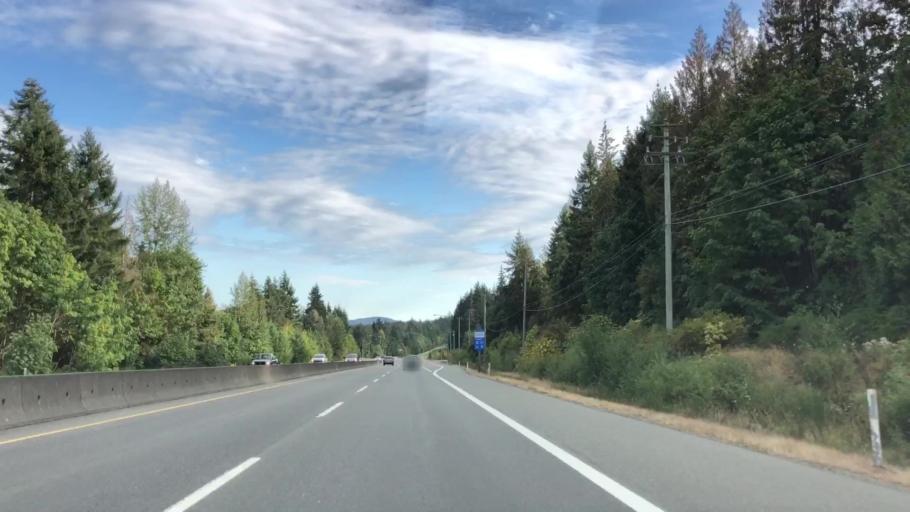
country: CA
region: British Columbia
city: North Saanich
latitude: 48.6171
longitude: -123.5429
